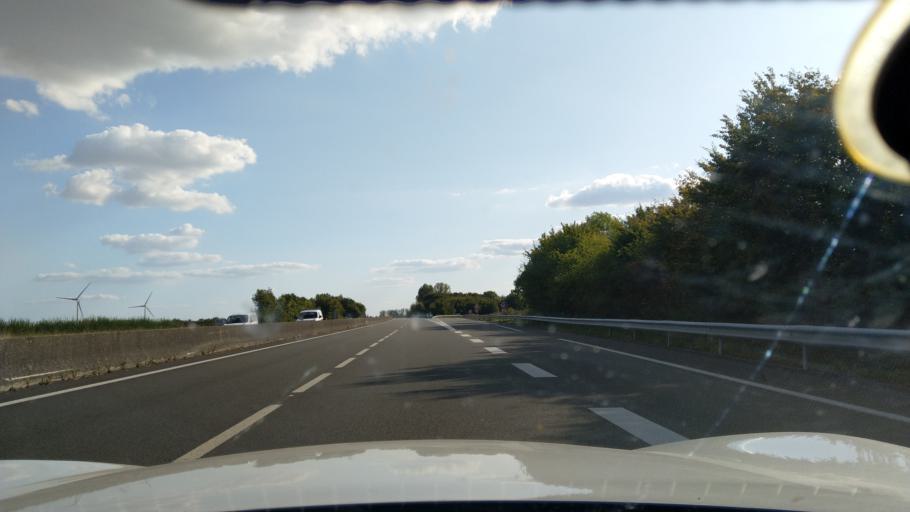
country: FR
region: Picardie
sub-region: Departement de l'Oise
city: Breteuil
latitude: 49.6076
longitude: 2.2054
